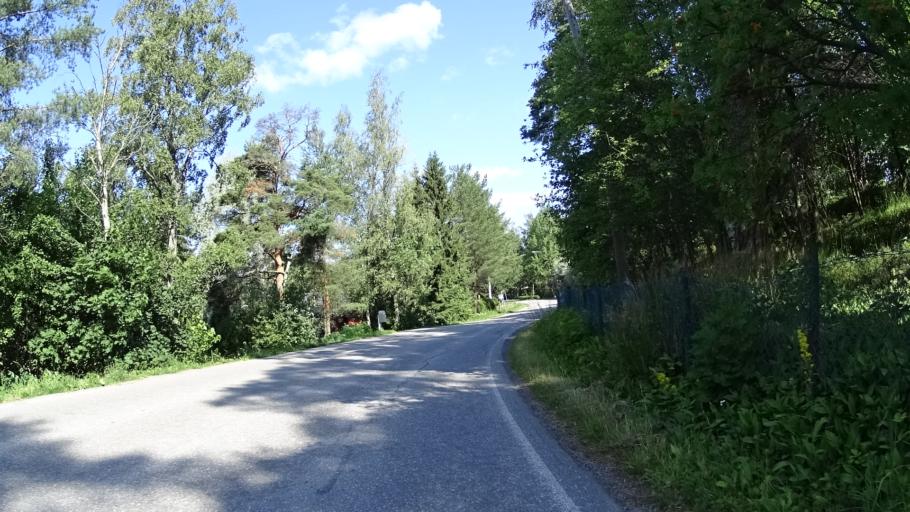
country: FI
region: Uusimaa
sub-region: Helsinki
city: Tuusula
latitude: 60.4213
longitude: 25.0493
